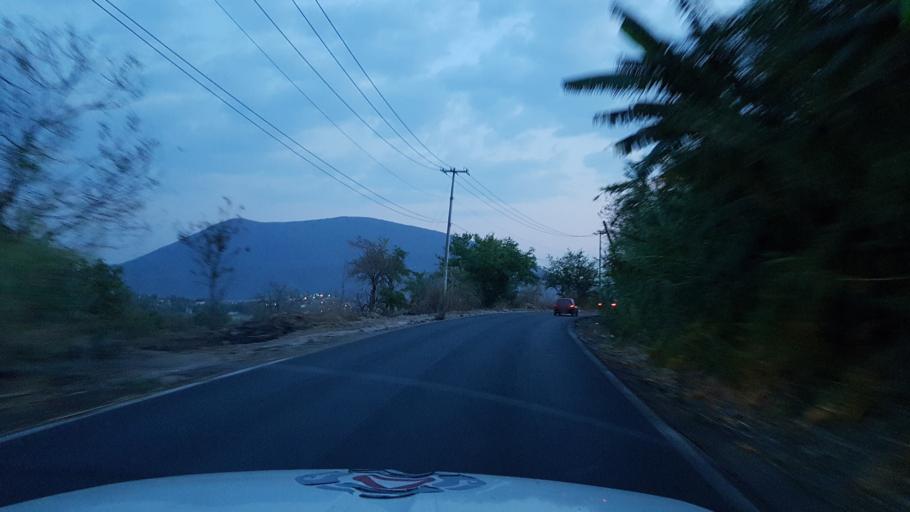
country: MX
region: Morelos
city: Tlaltizapan
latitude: 18.6905
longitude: -99.1326
